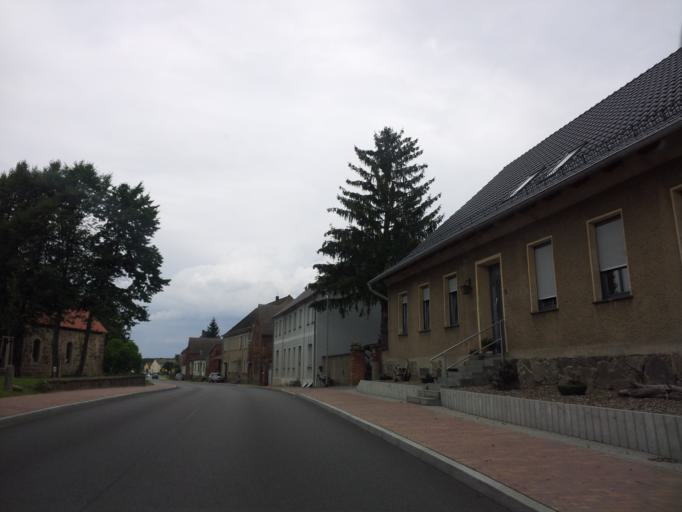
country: DE
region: Brandenburg
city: Niemegk
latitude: 52.0883
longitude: 12.7529
